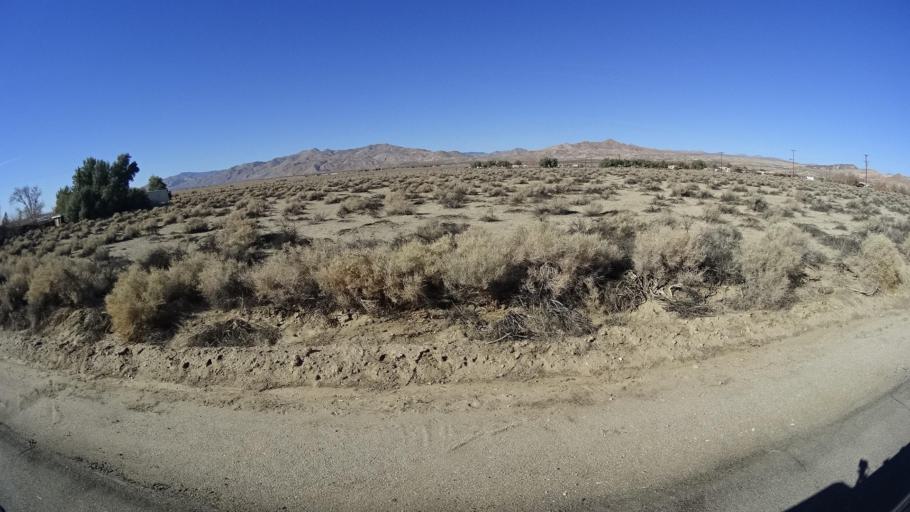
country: US
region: California
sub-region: Kern County
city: California City
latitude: 35.3076
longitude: -117.9503
